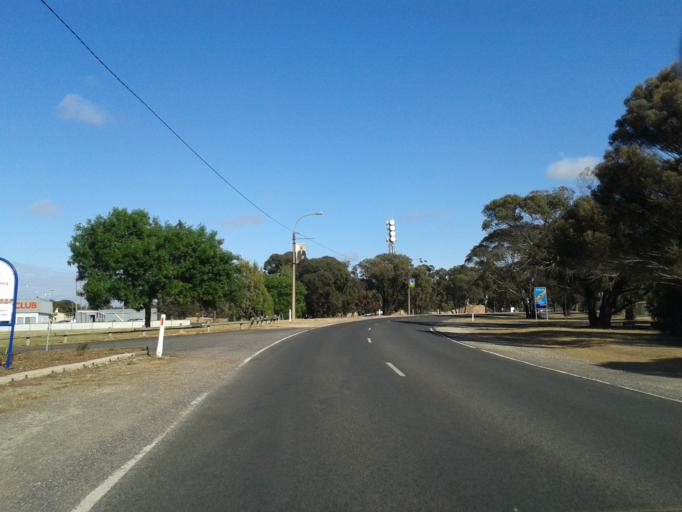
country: AU
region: South Australia
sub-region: Tatiara
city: Bordertown
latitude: -36.3078
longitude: 140.7693
